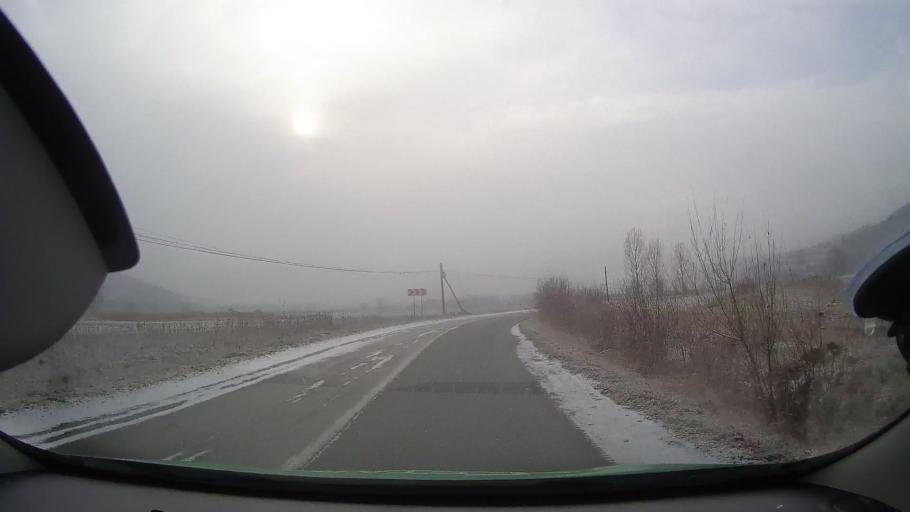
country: RO
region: Alba
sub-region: Comuna Rimetea
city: Rimetea
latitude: 46.4094
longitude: 23.5593
